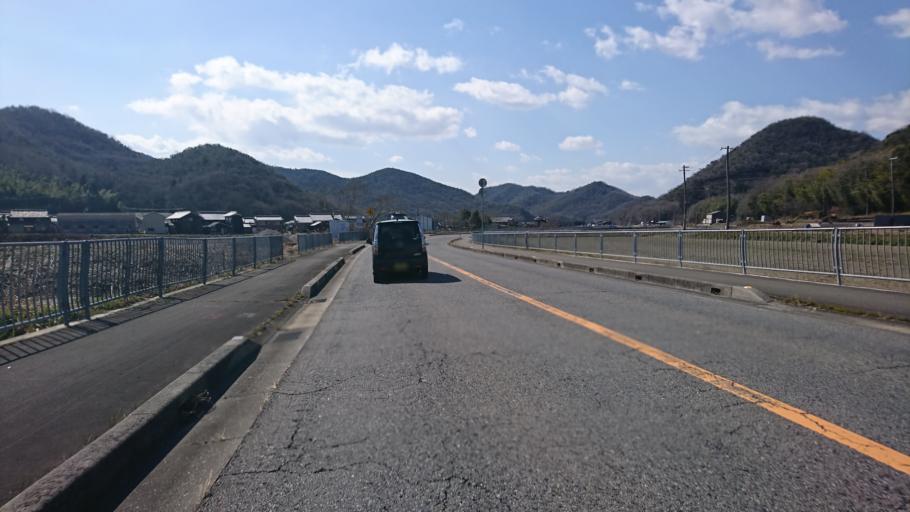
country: JP
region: Hyogo
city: Kakogawacho-honmachi
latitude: 34.8609
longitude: 134.7894
